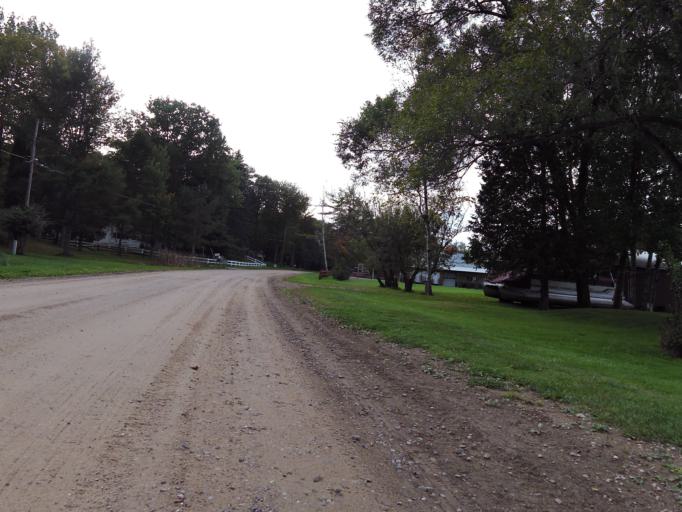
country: US
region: Michigan
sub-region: Roscommon County
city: Saint Helen
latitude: 44.3542
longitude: -84.4839
